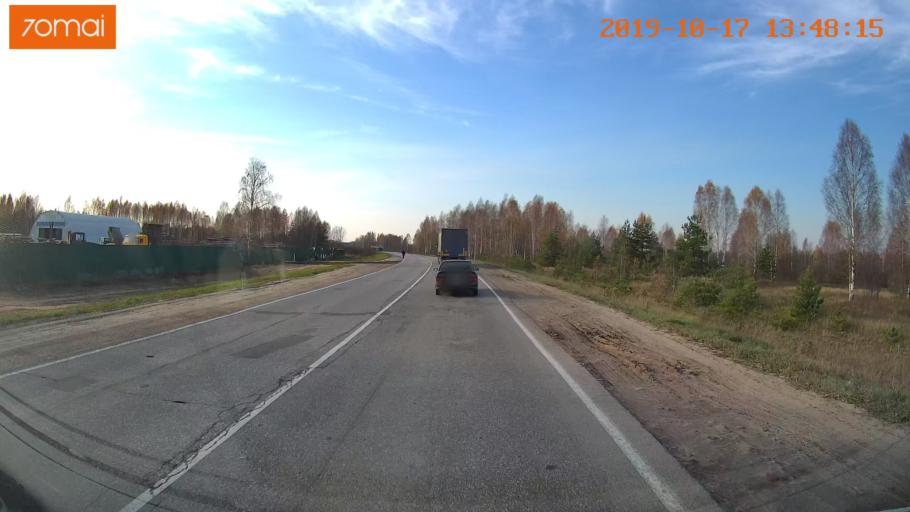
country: RU
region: Rjazan
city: Tuma
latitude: 55.1472
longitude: 40.4595
